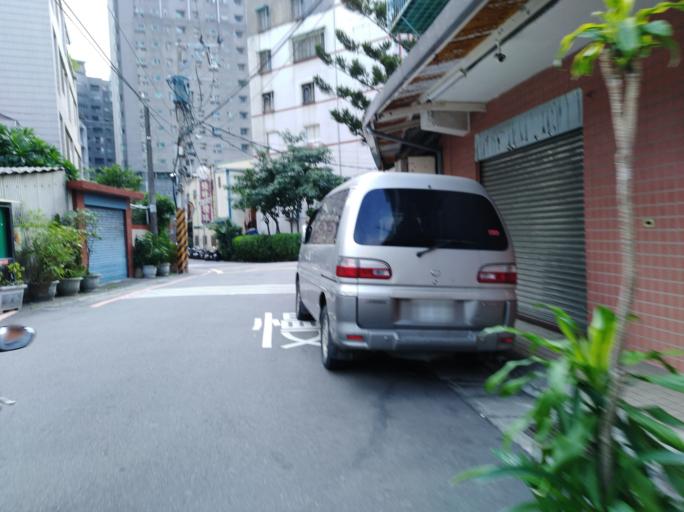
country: TW
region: Taipei
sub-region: Taipei
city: Banqiao
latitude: 25.0430
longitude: 121.4257
